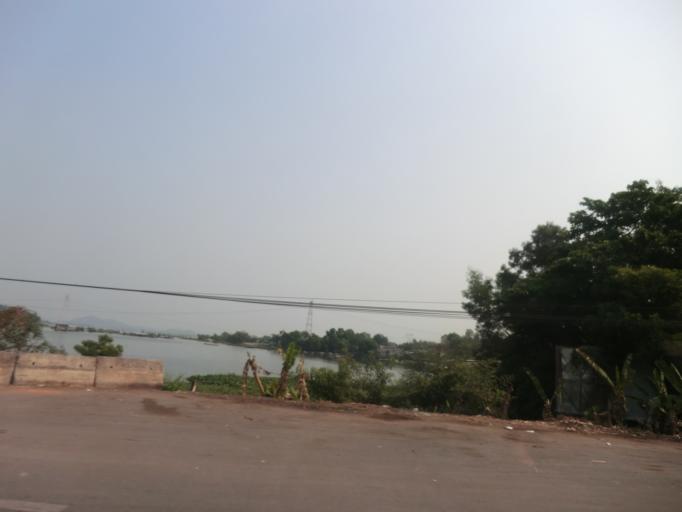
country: VN
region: Dong Nai
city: Tan Phu
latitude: 11.1577
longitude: 107.2729
